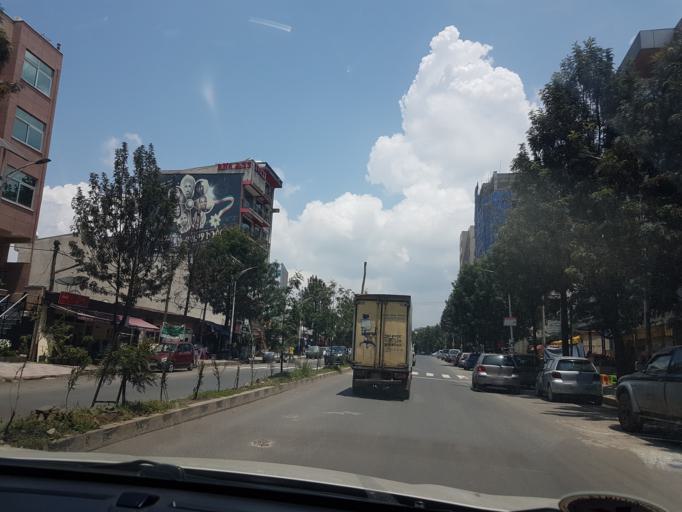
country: ET
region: Adis Abeba
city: Addis Ababa
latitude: 9.0032
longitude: 38.7980
